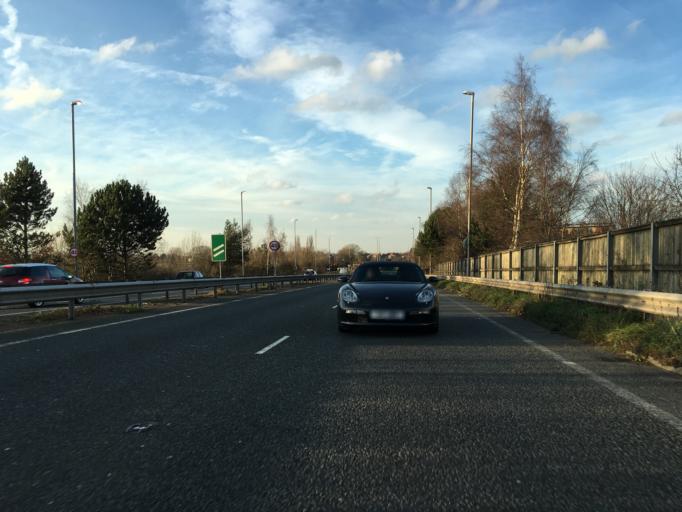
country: GB
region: England
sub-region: Borough of Stockport
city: Cheadle Hulme
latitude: 53.3648
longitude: -2.2060
